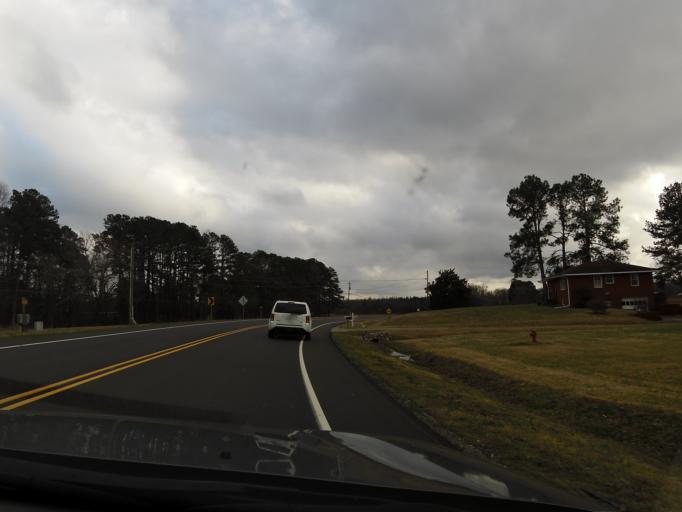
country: US
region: North Carolina
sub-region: Nash County
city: Rocky Mount
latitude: 35.9056
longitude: -77.7408
